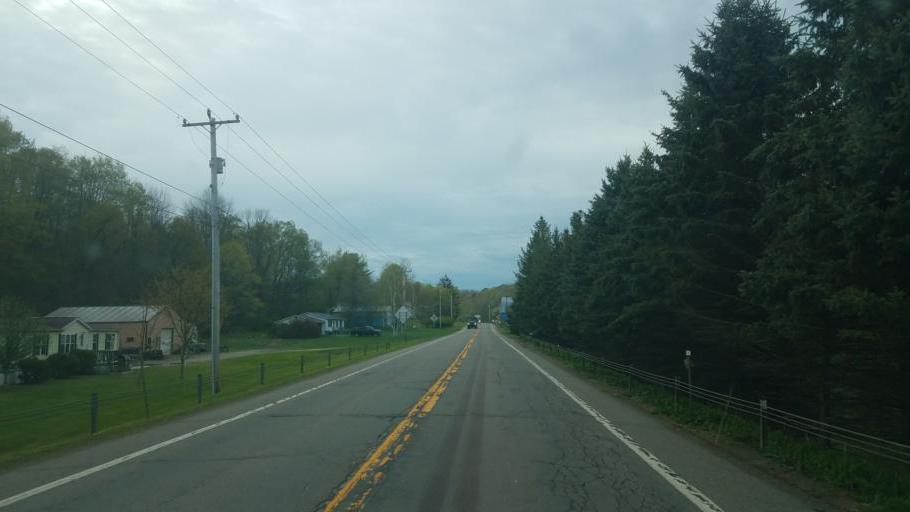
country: US
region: New York
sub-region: Steuben County
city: Canisteo
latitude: 42.2163
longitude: -77.5701
